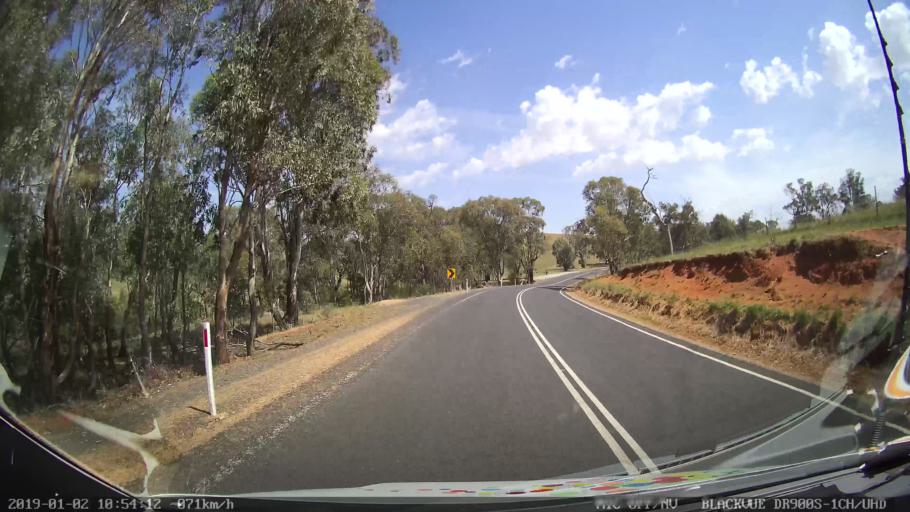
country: AU
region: New South Wales
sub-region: Cootamundra
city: Cootamundra
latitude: -34.6724
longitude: 148.2735
